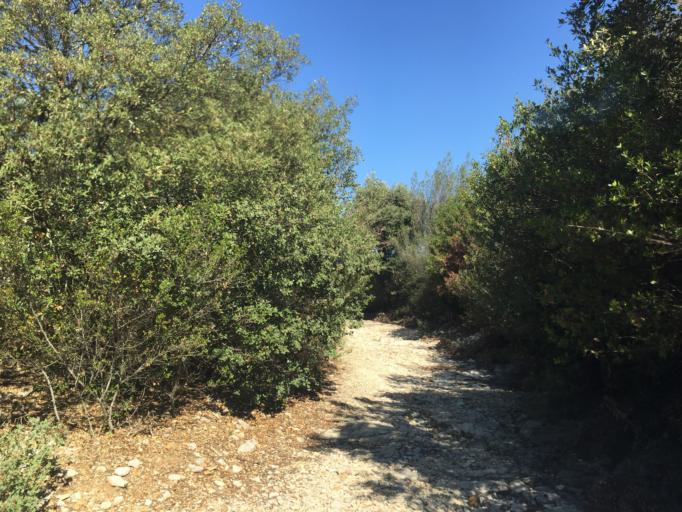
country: FR
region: Provence-Alpes-Cote d'Azur
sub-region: Departement du Vaucluse
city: Chateauneuf-du-Pape
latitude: 44.0704
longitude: 4.8199
